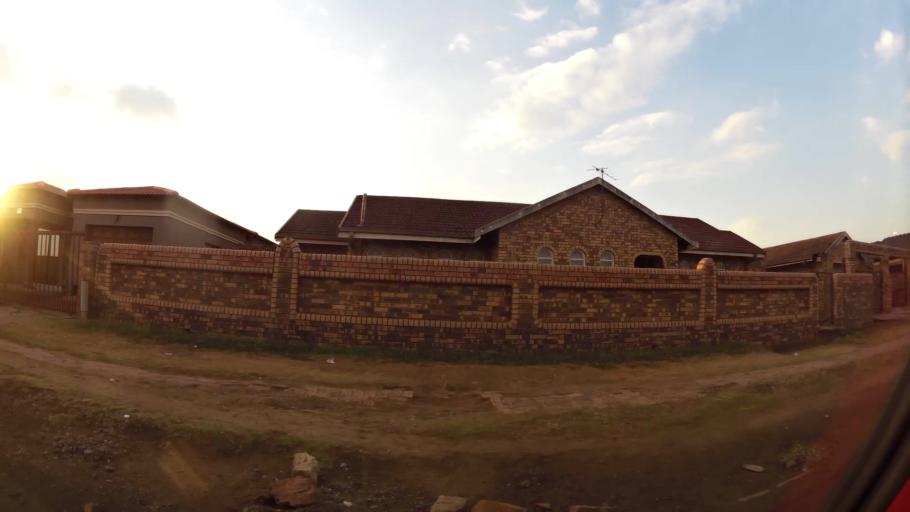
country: ZA
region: Gauteng
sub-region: City of Johannesburg Metropolitan Municipality
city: Orange Farm
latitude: -26.5933
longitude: 27.8431
